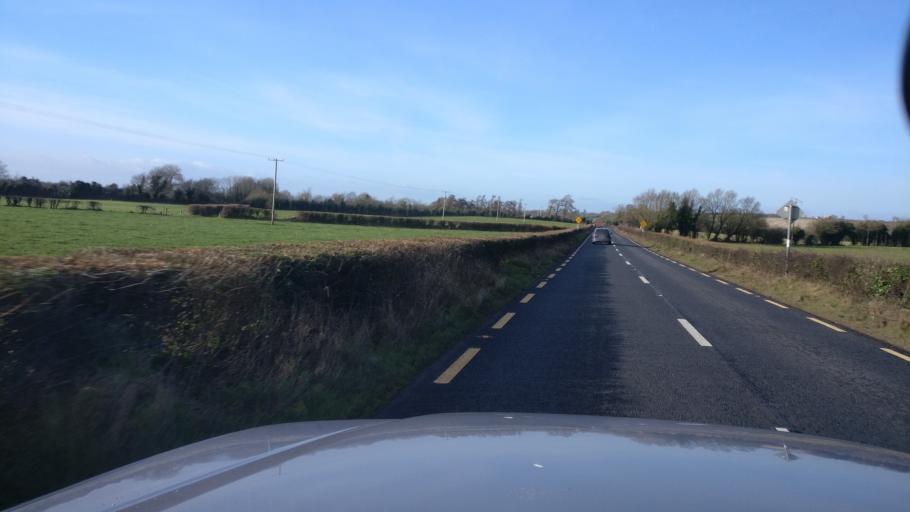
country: IE
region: Leinster
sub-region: Laois
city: Mountmellick
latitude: 53.1845
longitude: -7.3994
